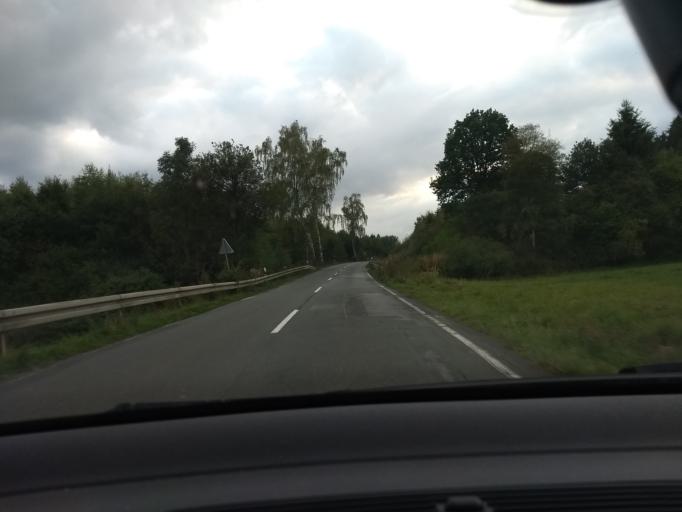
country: DE
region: North Rhine-Westphalia
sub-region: Regierungsbezirk Arnsberg
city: Arnsberg
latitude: 51.3534
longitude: 8.1458
